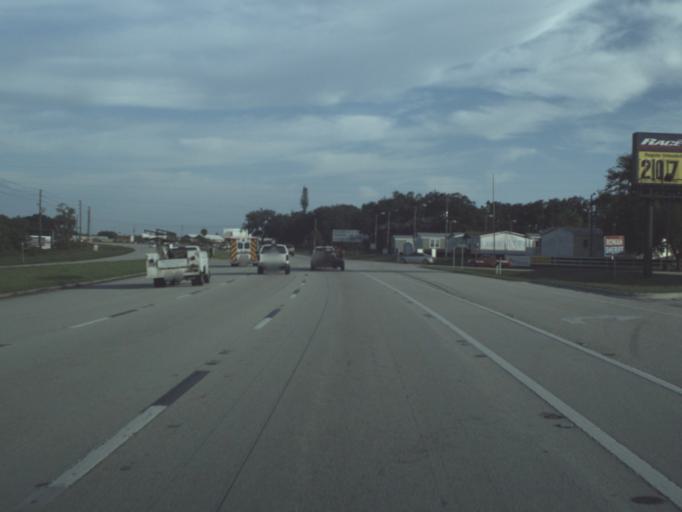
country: US
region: Florida
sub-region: Highlands County
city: Sebring
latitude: 27.4519
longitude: -81.4206
